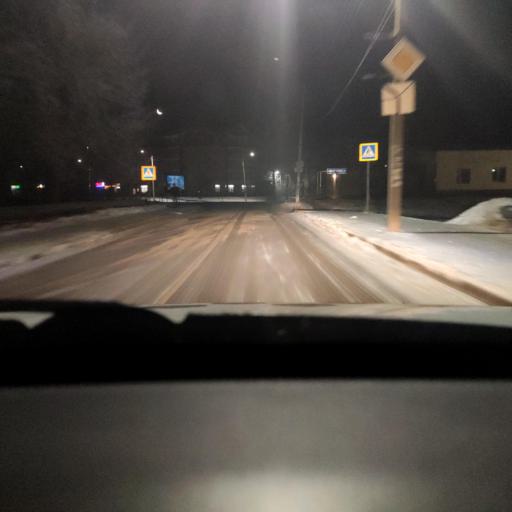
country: RU
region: Perm
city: Ust'-Kachka
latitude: 58.0039
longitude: 55.6742
